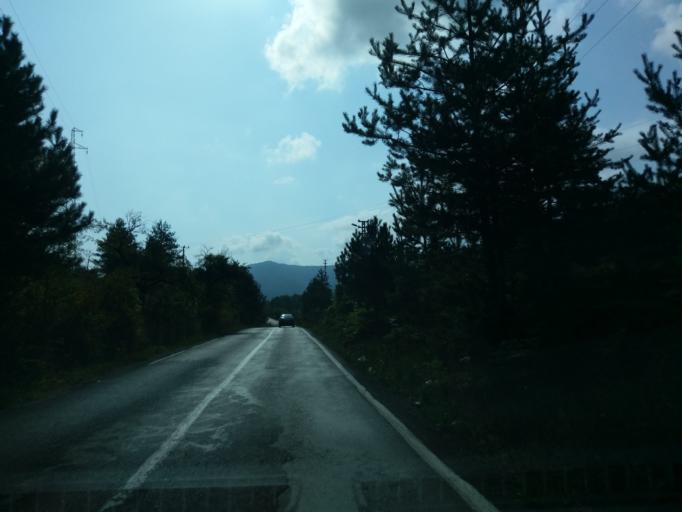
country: TR
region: Sinop
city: Ayancik
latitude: 41.8799
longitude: 34.5267
